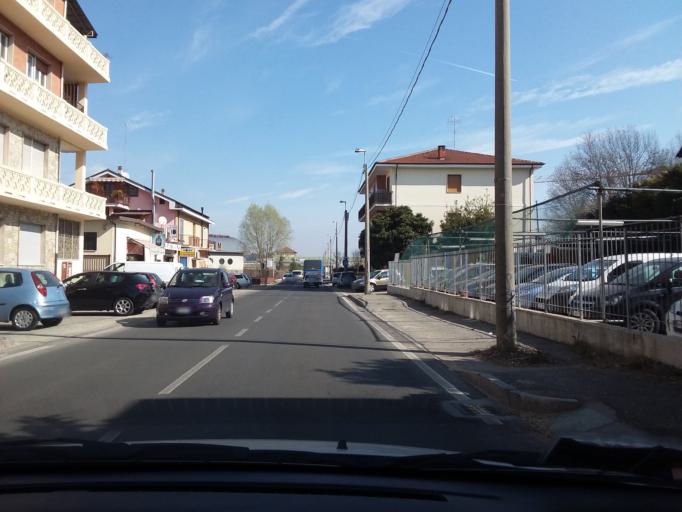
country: IT
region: Piedmont
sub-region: Provincia di Torino
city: Rivoli
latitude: 45.0823
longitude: 7.5188
